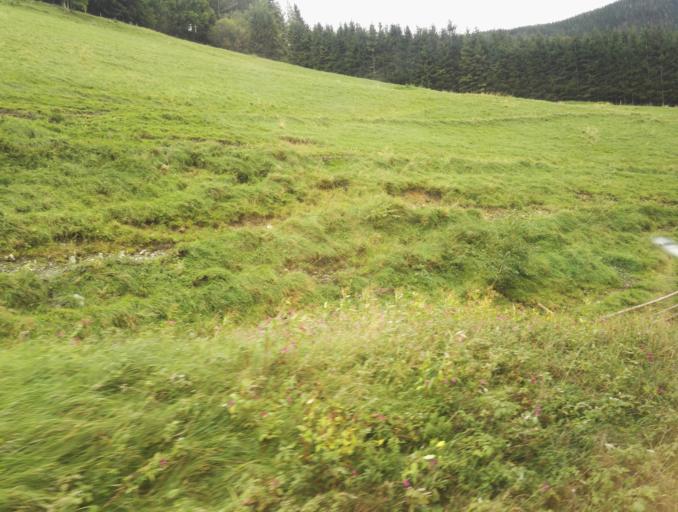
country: AT
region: Styria
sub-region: Politischer Bezirk Leoben
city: Vordernberg
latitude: 47.4896
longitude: 14.9967
